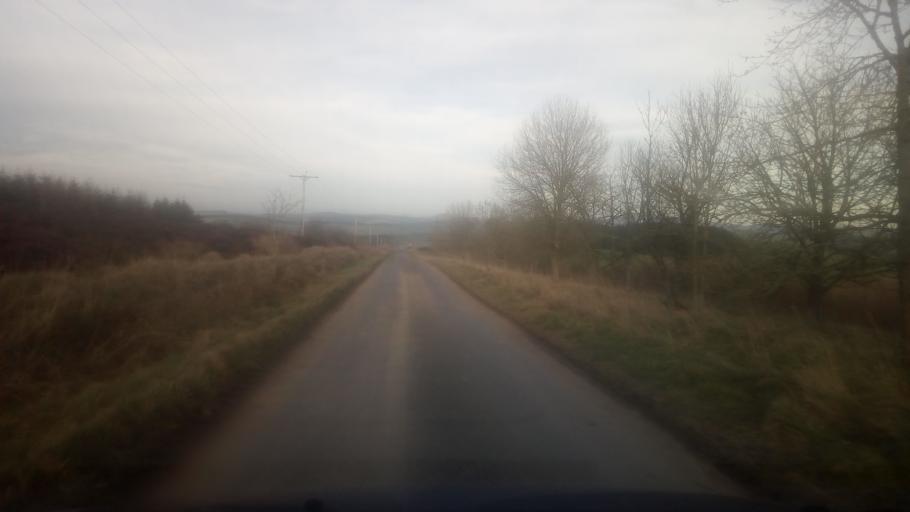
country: GB
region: Scotland
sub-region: The Scottish Borders
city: Jedburgh
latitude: 55.3988
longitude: -2.5408
